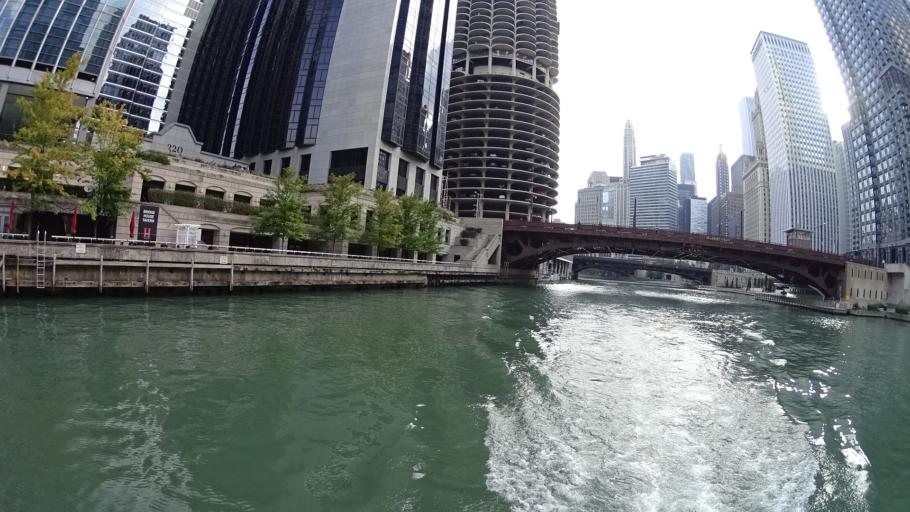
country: US
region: Illinois
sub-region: Cook County
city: Chicago
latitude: 41.8876
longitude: -87.6304
